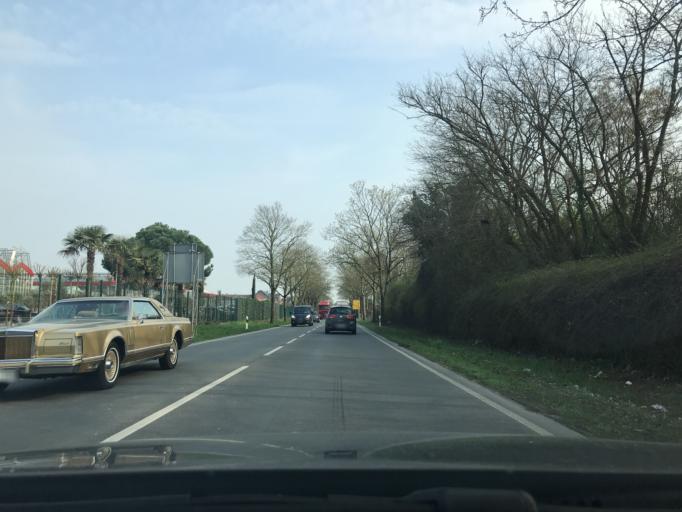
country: DE
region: North Rhine-Westphalia
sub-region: Regierungsbezirk Dusseldorf
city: Kevelaer
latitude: 51.5881
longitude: 6.2476
